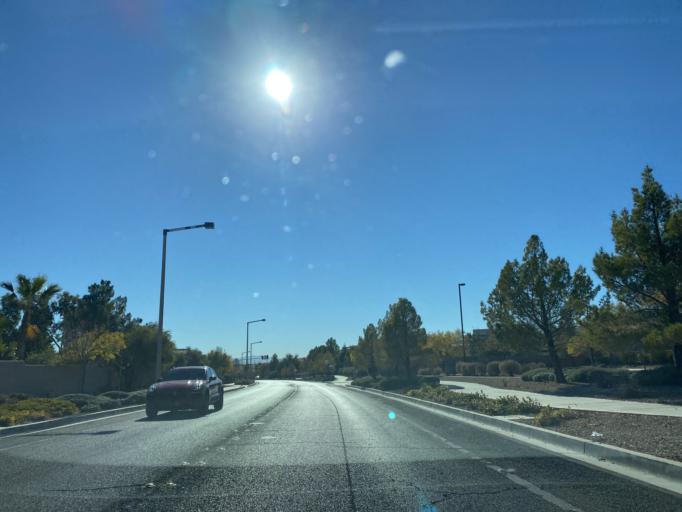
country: US
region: Nevada
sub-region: Clark County
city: Summerlin South
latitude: 36.1677
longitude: -115.3430
